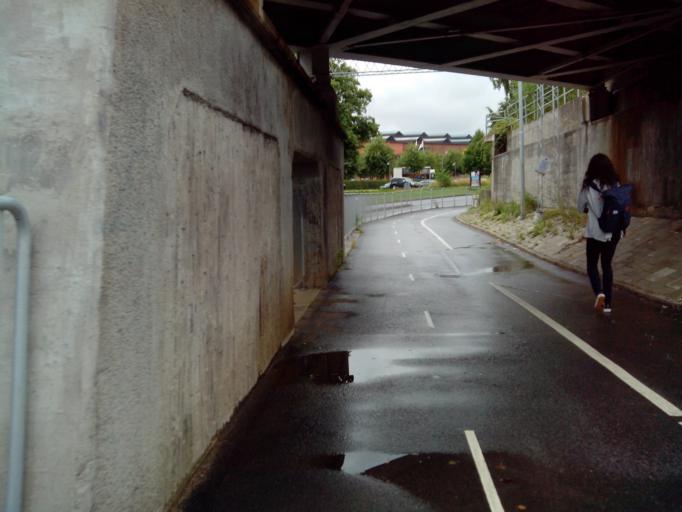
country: SE
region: Vaestra Goetaland
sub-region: Goteborg
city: Goeteborg
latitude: 57.7127
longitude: 11.9433
